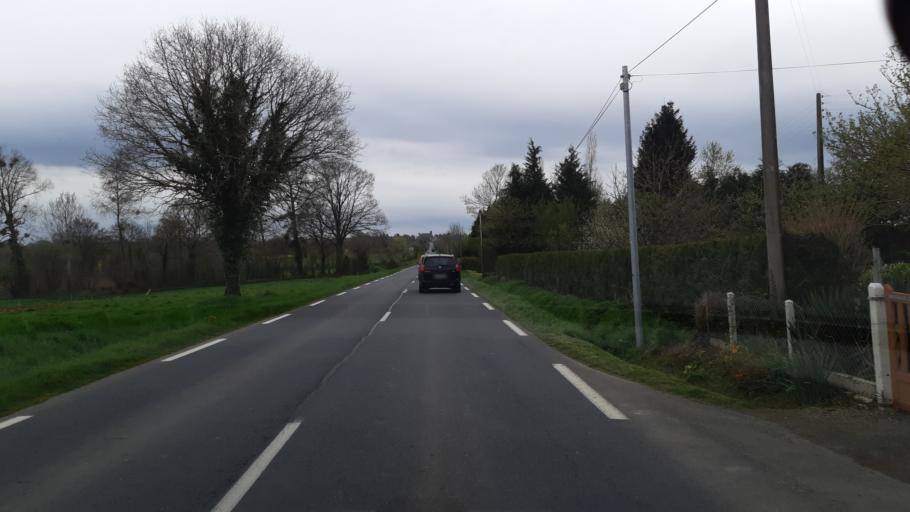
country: FR
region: Lower Normandy
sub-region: Departement de la Manche
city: Percy
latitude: 48.9740
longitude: -1.1623
